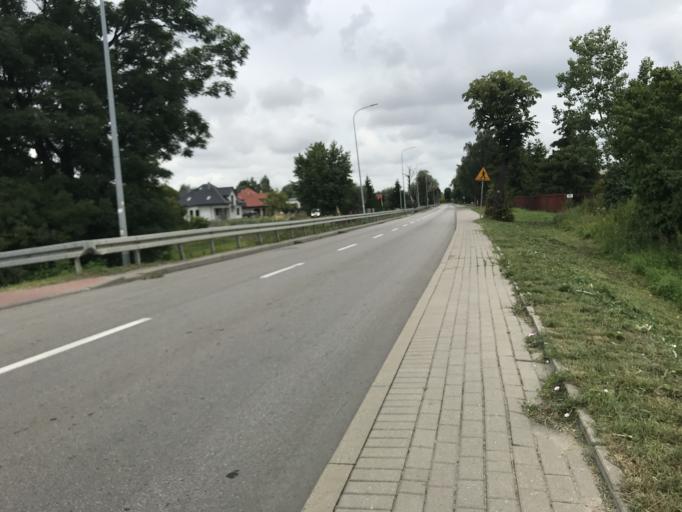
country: PL
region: Warmian-Masurian Voivodeship
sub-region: Powiat elblaski
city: Elblag
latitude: 54.1665
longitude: 19.3890
